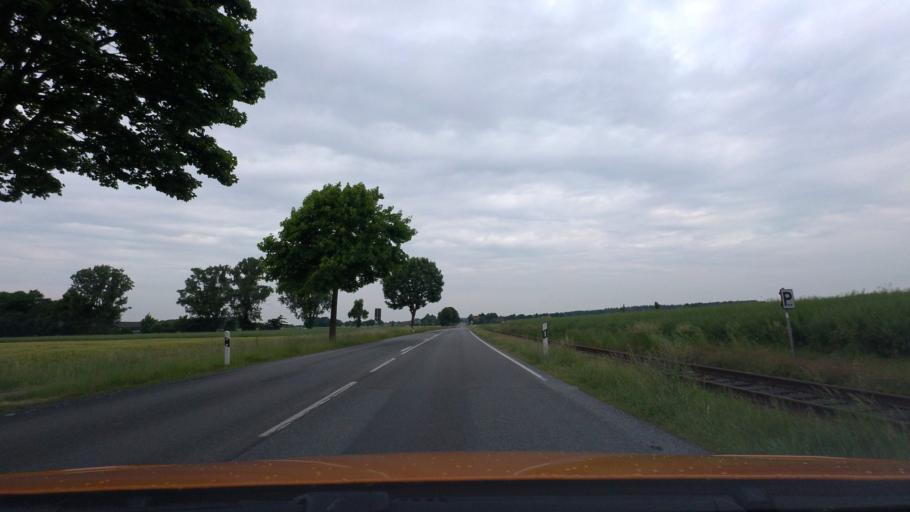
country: DE
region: Lower Saxony
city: Syke
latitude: 52.8894
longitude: 8.8490
